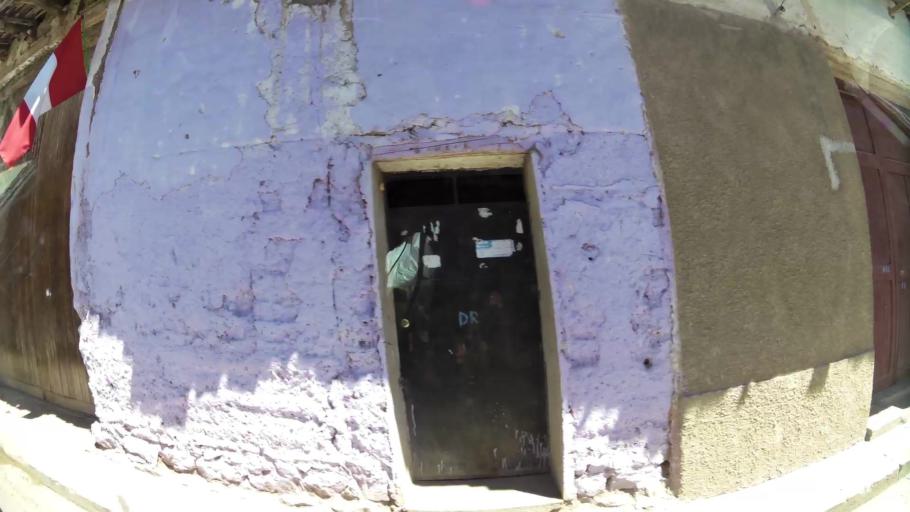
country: PE
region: Junin
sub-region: Provincia de Jauja
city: Jauja
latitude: -11.7729
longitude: -75.5015
